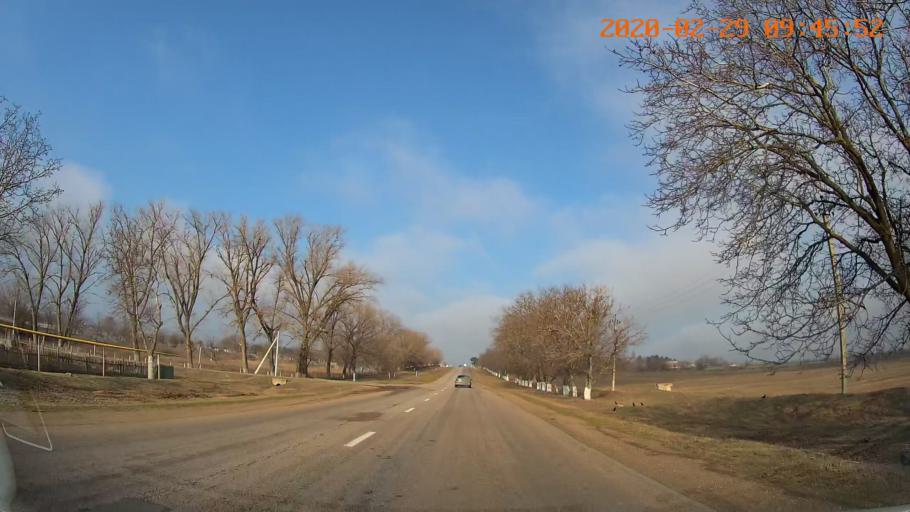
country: MD
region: Telenesti
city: Crasnoe
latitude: 46.6624
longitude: 29.8053
